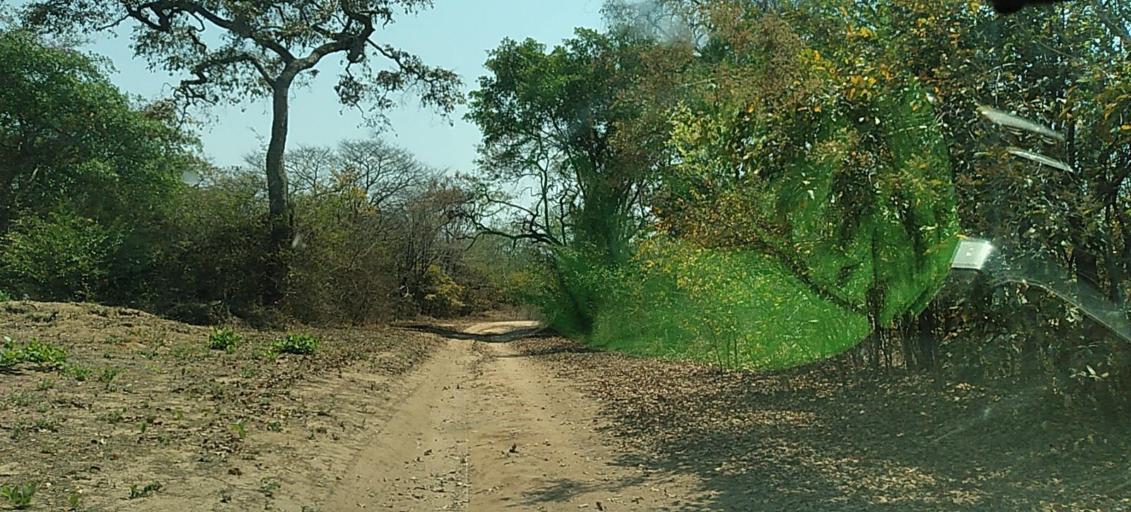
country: ZM
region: North-Western
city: Kalengwa
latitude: -13.1017
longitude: 24.6922
